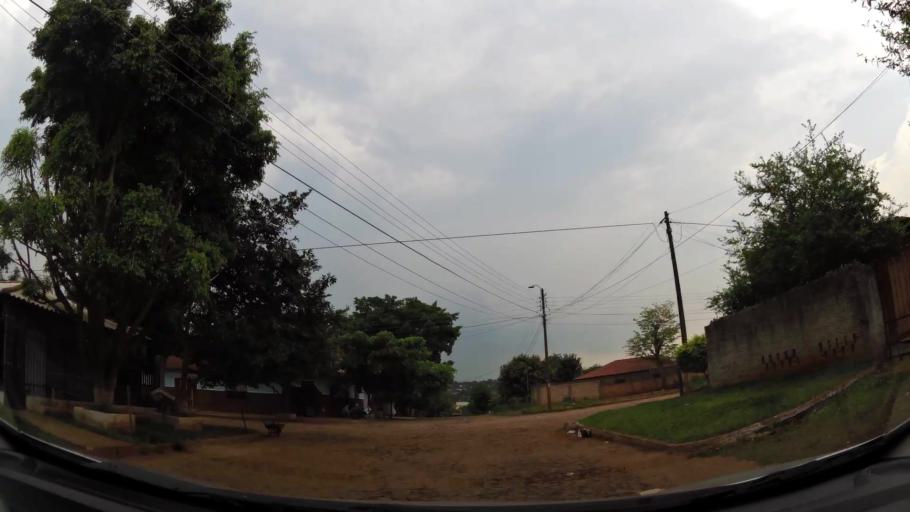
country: BR
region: Parana
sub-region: Foz Do Iguacu
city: Foz do Iguacu
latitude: -25.5468
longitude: -54.6023
